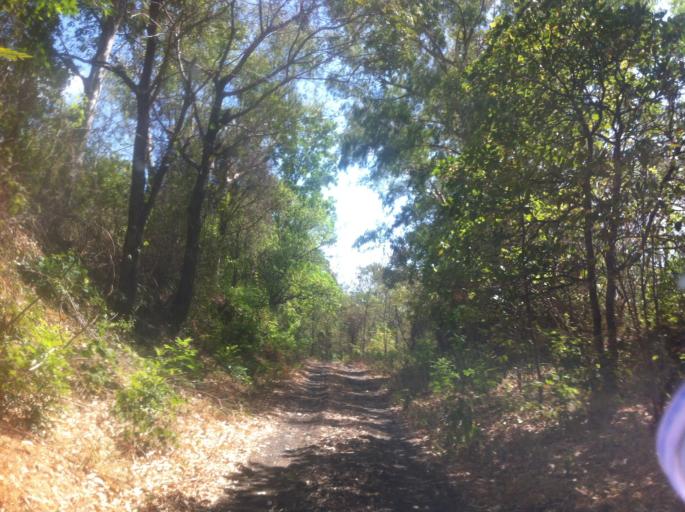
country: NI
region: Chinandega
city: Chichigalpa
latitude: 12.6957
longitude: -87.0282
